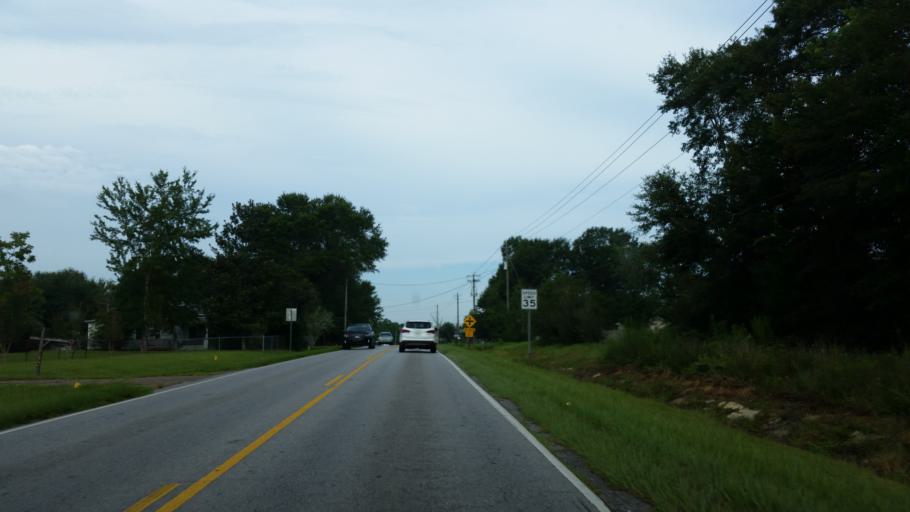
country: US
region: Florida
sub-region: Escambia County
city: Gonzalez
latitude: 30.5633
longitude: -87.3072
